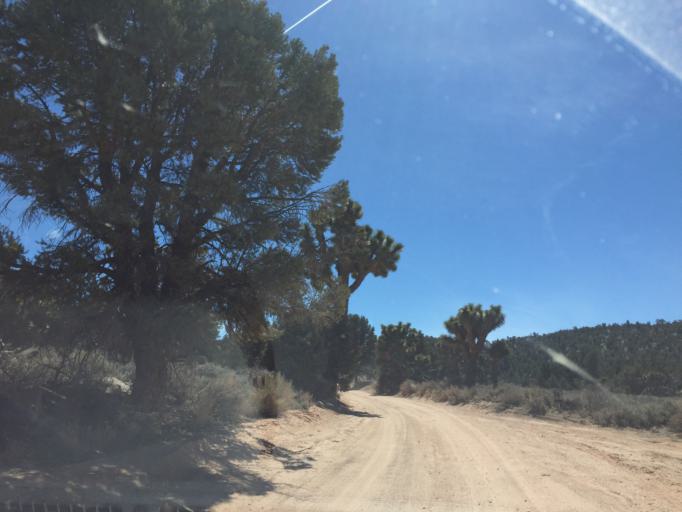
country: US
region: California
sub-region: San Bernardino County
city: Big Bear City
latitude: 34.2476
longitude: -116.7043
